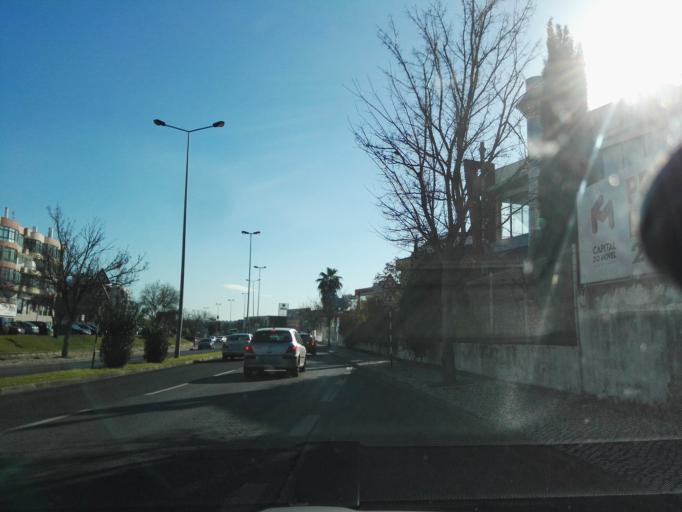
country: PT
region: Setubal
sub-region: Seixal
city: Corroios
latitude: 38.6542
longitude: -9.1667
